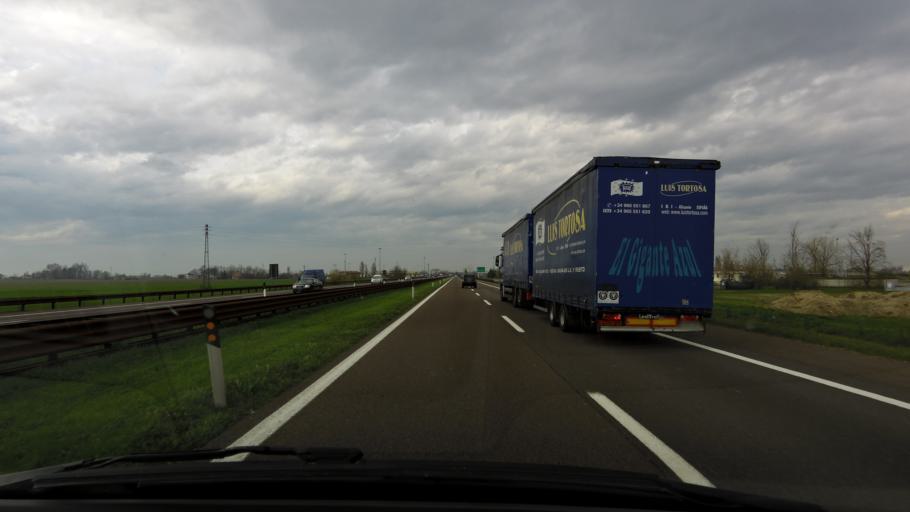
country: IT
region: Emilia-Romagna
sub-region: Provincia di Modena
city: Campogalliano
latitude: 44.6979
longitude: 10.8499
